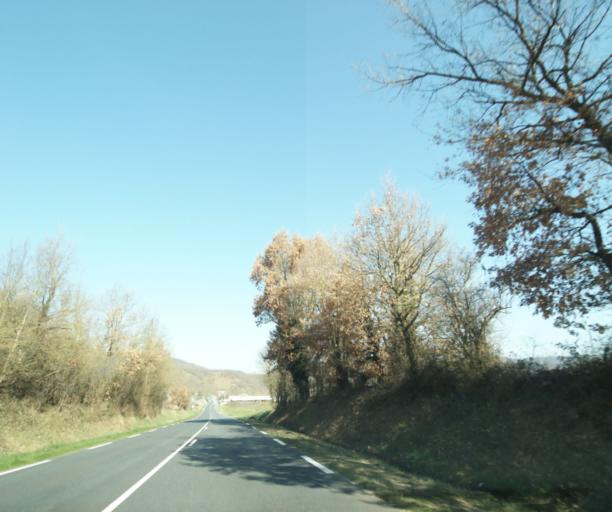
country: FR
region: Midi-Pyrenees
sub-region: Departement de l'Aveyron
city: Saint-Affrique
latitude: 43.9336
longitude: 2.8289
